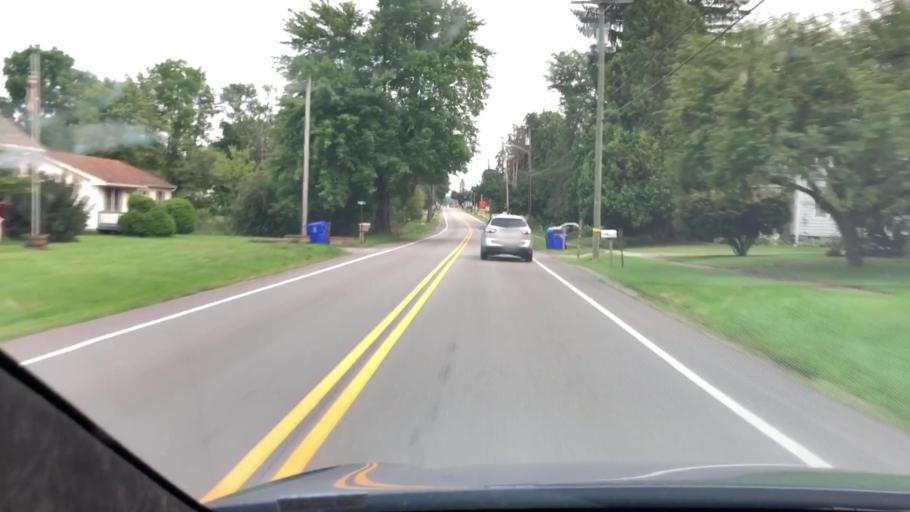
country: US
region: Pennsylvania
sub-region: Mercer County
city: Grove City
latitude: 41.1411
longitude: -80.0095
